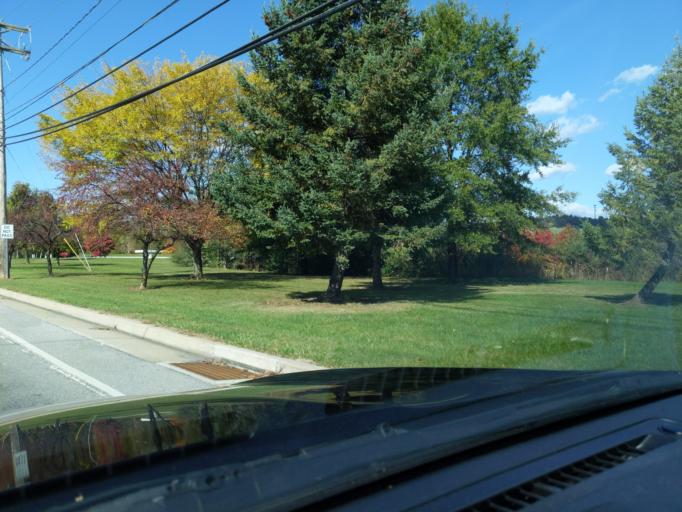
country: US
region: Pennsylvania
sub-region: Blair County
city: Duncansville
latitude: 40.4377
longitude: -78.4132
